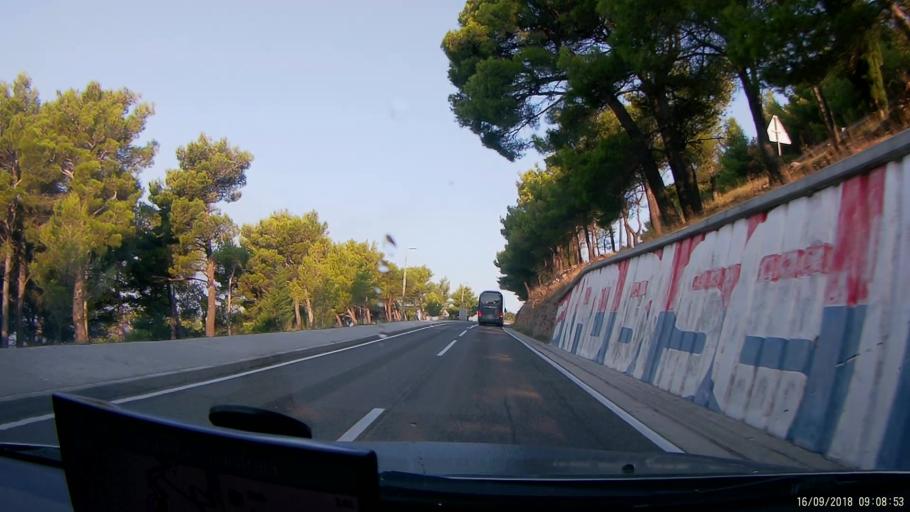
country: HR
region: Splitsko-Dalmatinska
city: Donja Brela
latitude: 43.3736
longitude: 16.9275
